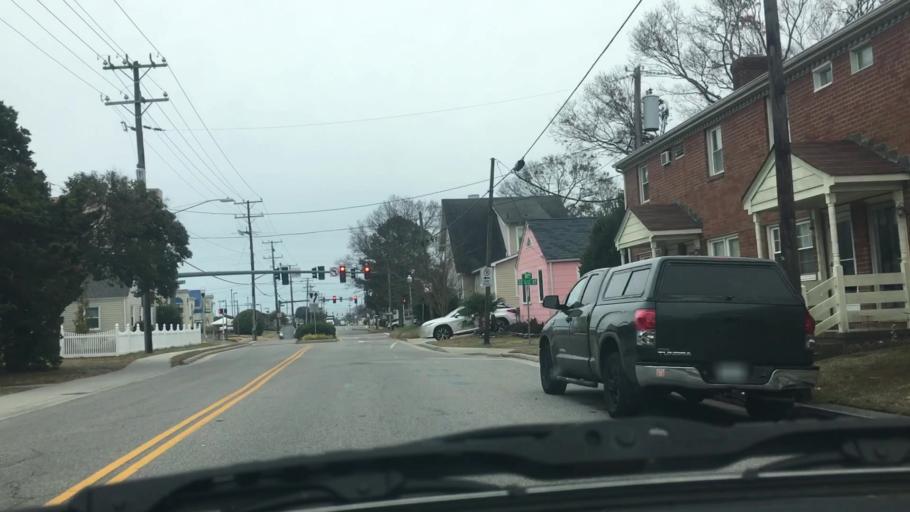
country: US
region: Virginia
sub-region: City of Virginia Beach
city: Virginia Beach
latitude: 36.8505
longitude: -75.9789
